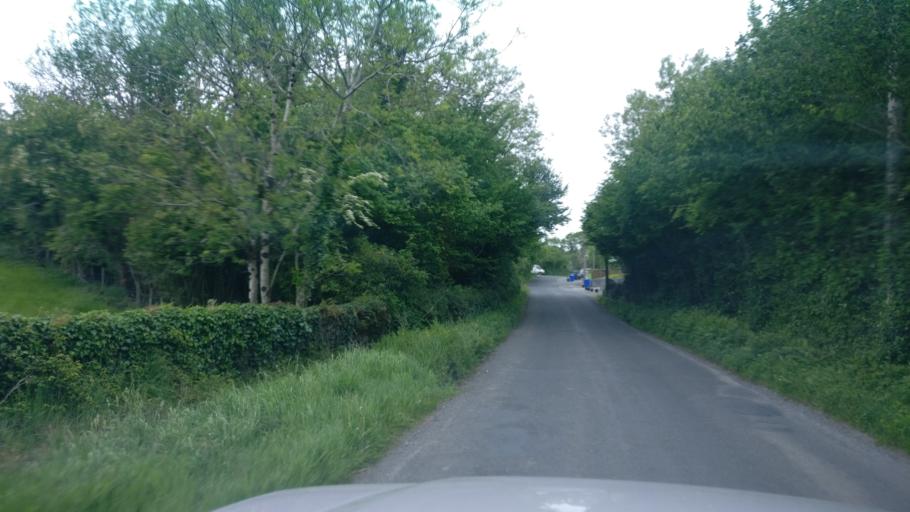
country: IE
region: Connaught
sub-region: County Galway
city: Loughrea
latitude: 53.1114
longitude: -8.4067
